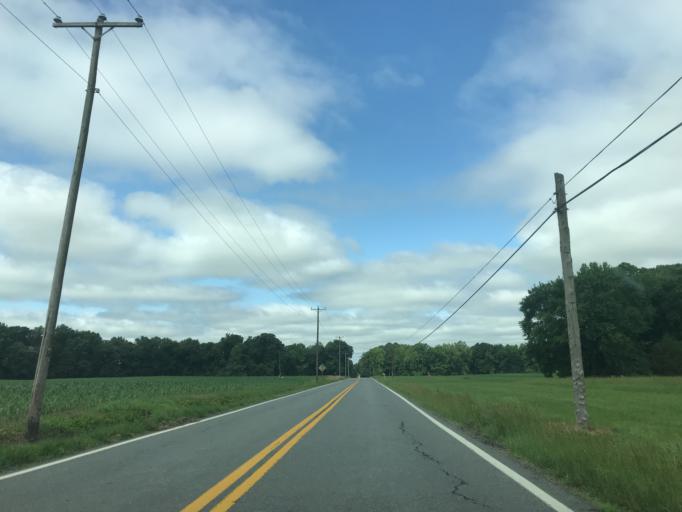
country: US
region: Maryland
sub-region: Caroline County
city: Ridgely
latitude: 38.8858
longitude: -75.9623
